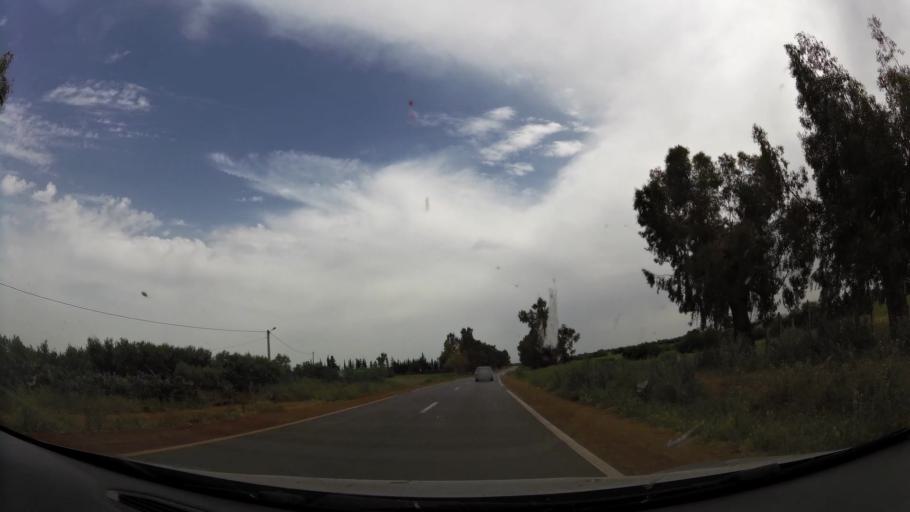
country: MA
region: Rabat-Sale-Zemmour-Zaer
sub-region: Khemisset
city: Tiflet
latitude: 33.8338
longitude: -6.2719
